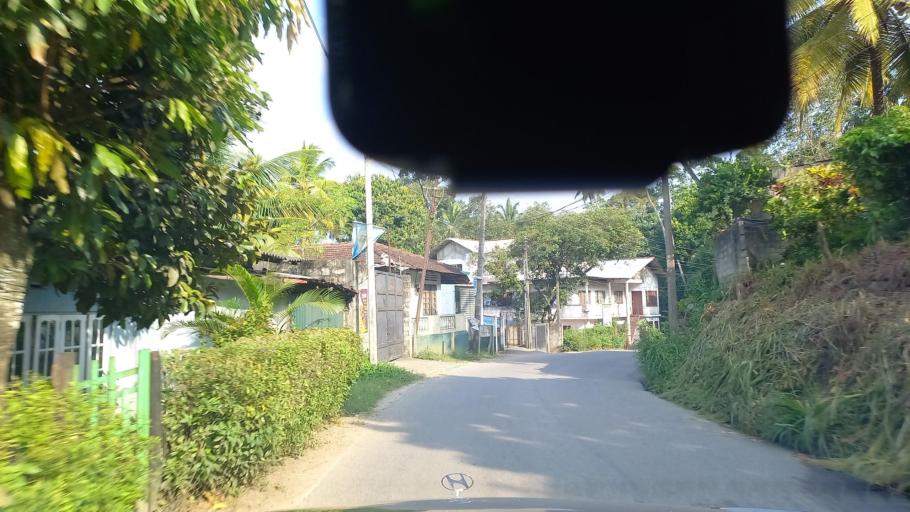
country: LK
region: Central
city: Kandy
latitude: 7.2423
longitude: 80.5992
